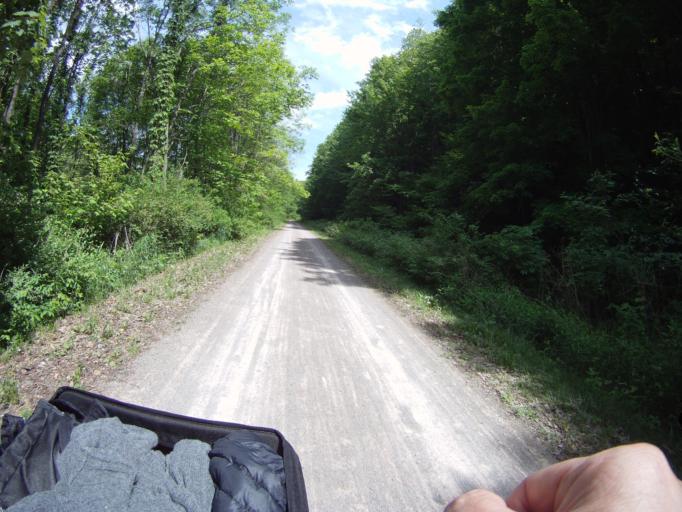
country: US
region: Pennsylvania
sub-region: Somerset County
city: Meyersdale
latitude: 39.8079
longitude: -78.9906
